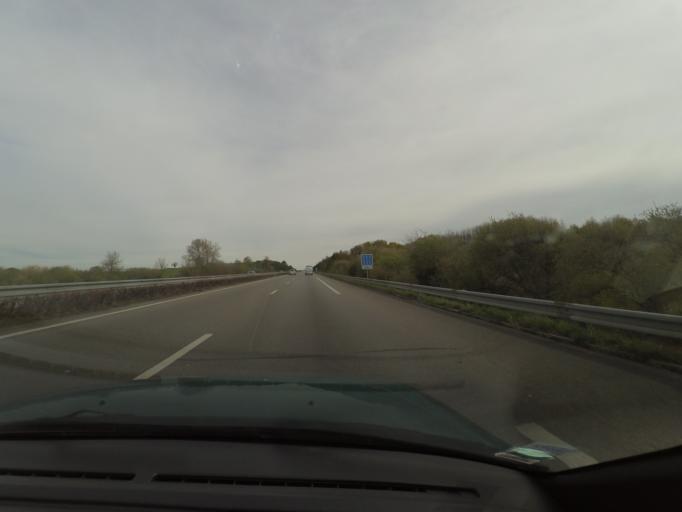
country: FR
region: Pays de la Loire
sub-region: Departement de la Loire-Atlantique
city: Mauves-sur-Loire
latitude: 47.3153
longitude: -1.4110
